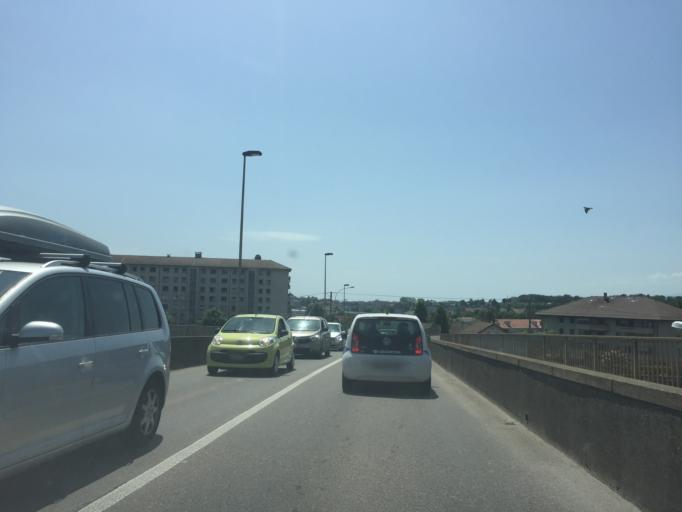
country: CH
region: Vaud
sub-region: Ouest Lausannois District
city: Chavannes
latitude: 46.5400
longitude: 6.5757
